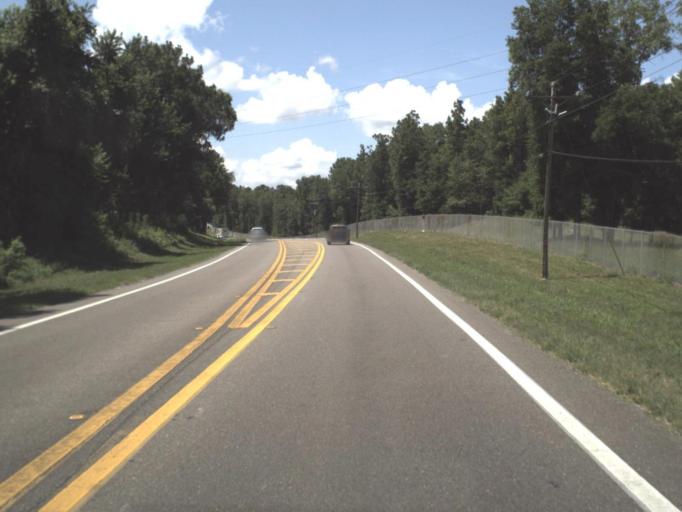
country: US
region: Florida
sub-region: Clay County
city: Keystone Heights
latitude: 29.7606
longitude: -82.0560
